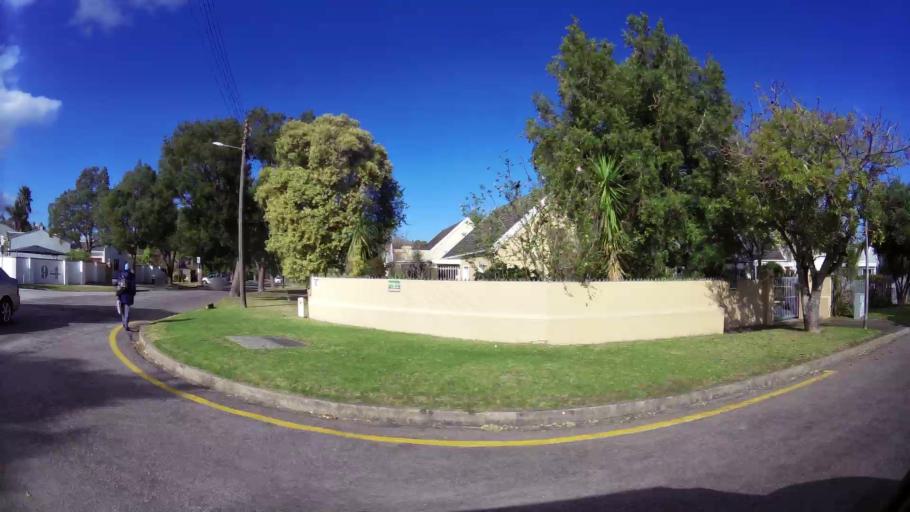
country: ZA
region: Western Cape
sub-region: Eden District Municipality
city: George
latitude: -33.9597
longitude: 22.4858
